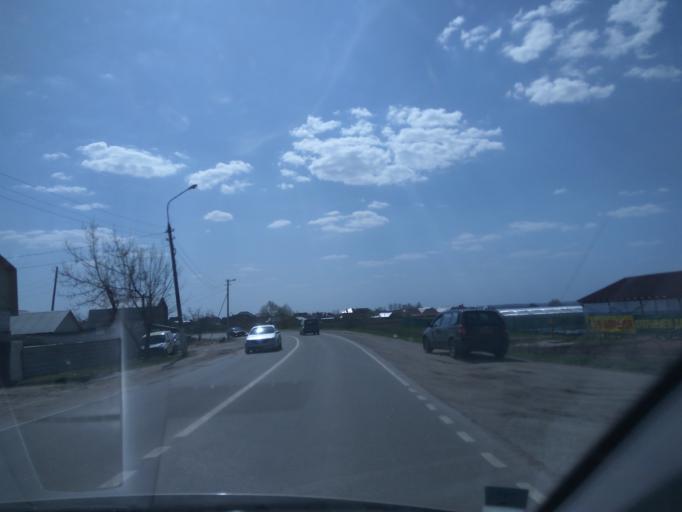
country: RU
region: Moskovskaya
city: Ramenskoye
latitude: 55.5479
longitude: 38.2336
